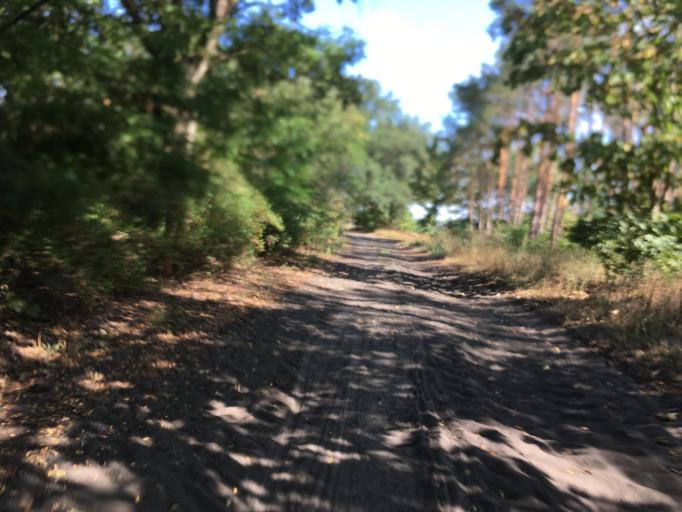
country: DE
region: Brandenburg
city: Zehdenick
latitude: 52.9665
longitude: 13.3840
